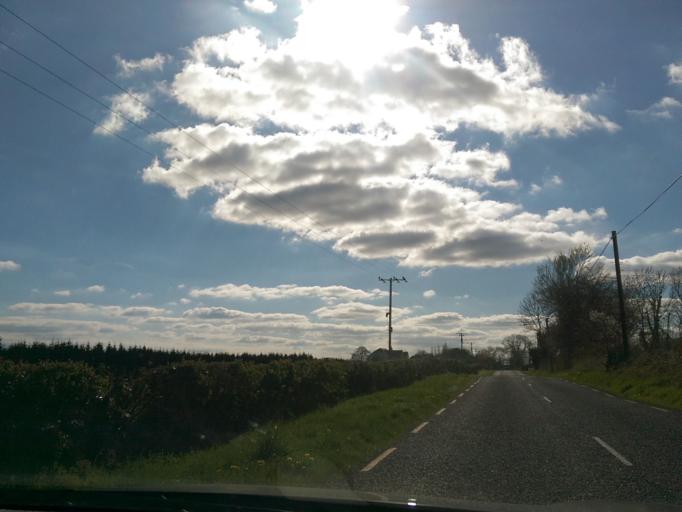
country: IE
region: Leinster
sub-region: Uibh Fhaili
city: Birr
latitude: 53.1039
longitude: -7.7941
